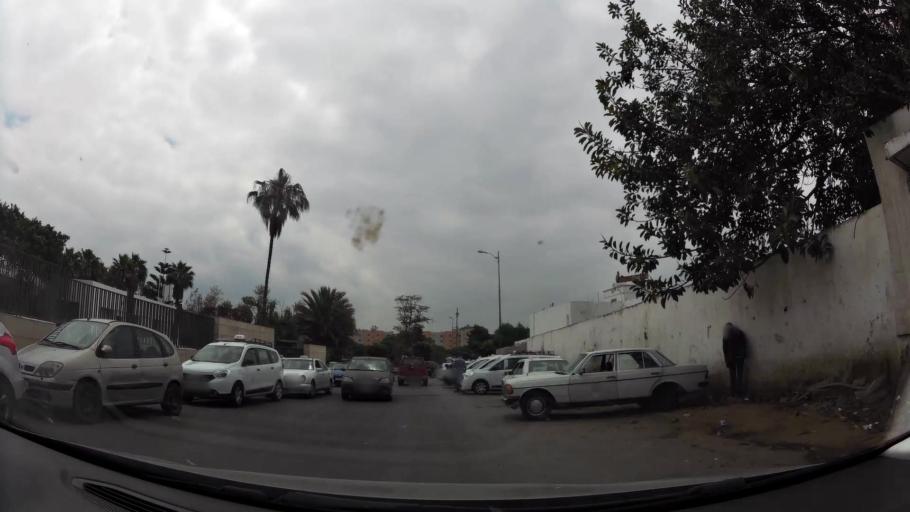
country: MA
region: Rabat-Sale-Zemmour-Zaer
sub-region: Rabat
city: Rabat
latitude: 33.9885
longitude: -6.8690
